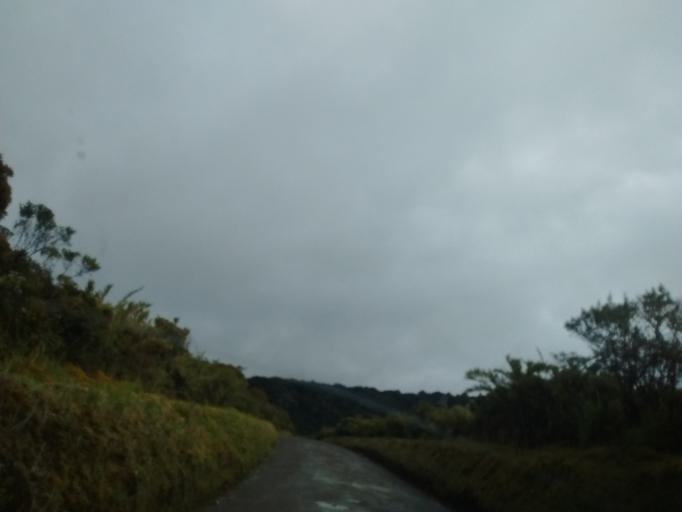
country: CO
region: Cauca
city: Totoro
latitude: 2.3546
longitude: -76.3405
